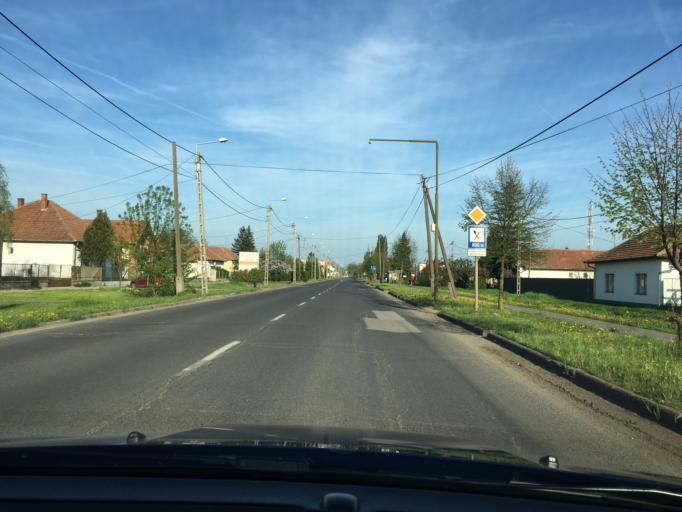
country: HU
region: Bekes
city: Szeghalom
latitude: 47.0165
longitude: 21.1634
